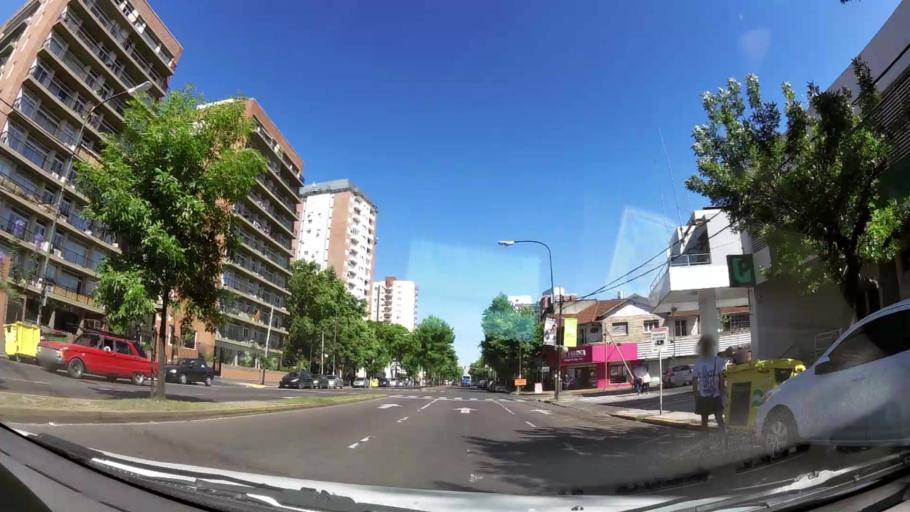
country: AR
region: Buenos Aires
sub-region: Partido de San Isidro
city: San Isidro
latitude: -34.4608
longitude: -58.5277
